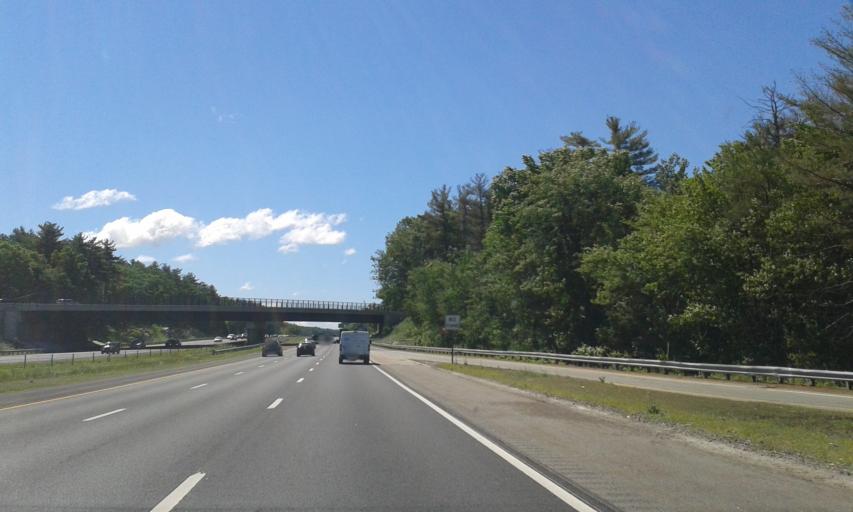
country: US
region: Massachusetts
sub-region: Middlesex County
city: Billerica
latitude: 42.5619
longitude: -71.2989
